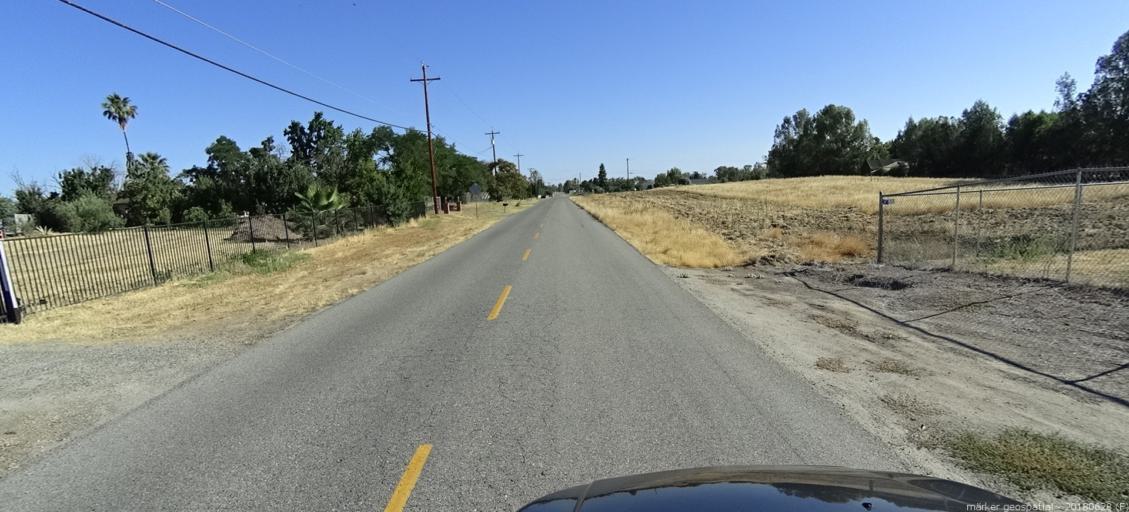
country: US
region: California
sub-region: Madera County
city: Bonadelle Ranchos-Madera Ranchos
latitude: 36.9680
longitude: -119.8853
